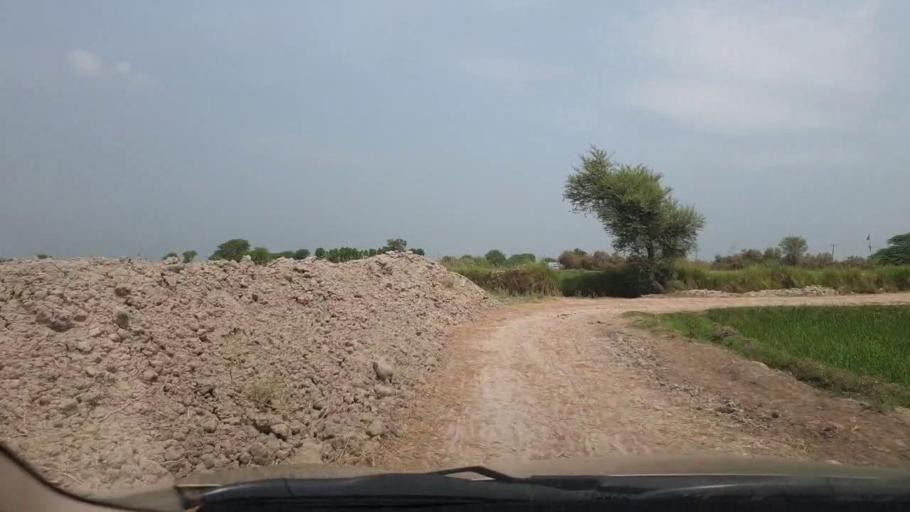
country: PK
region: Sindh
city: Goth Garelo
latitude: 27.5211
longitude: 68.1214
